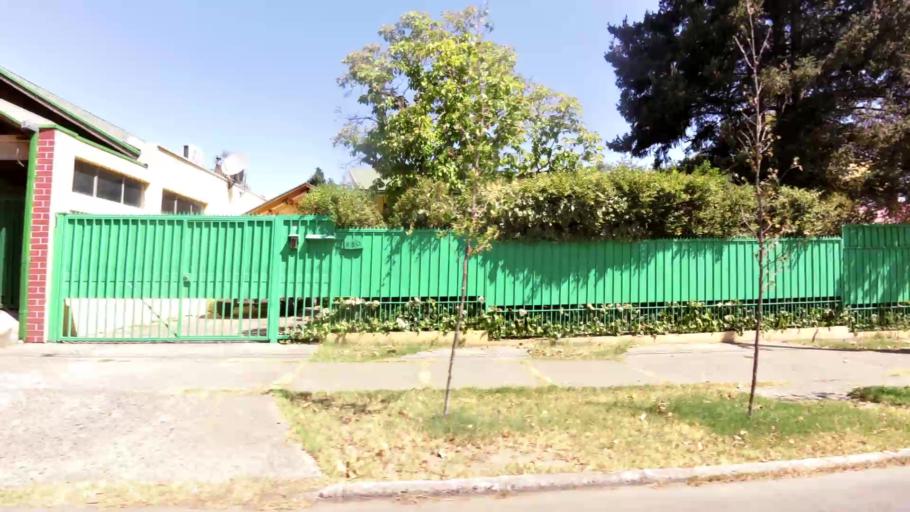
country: CL
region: Maule
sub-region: Provincia de Talca
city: Talca
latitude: -35.4169
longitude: -71.6623
